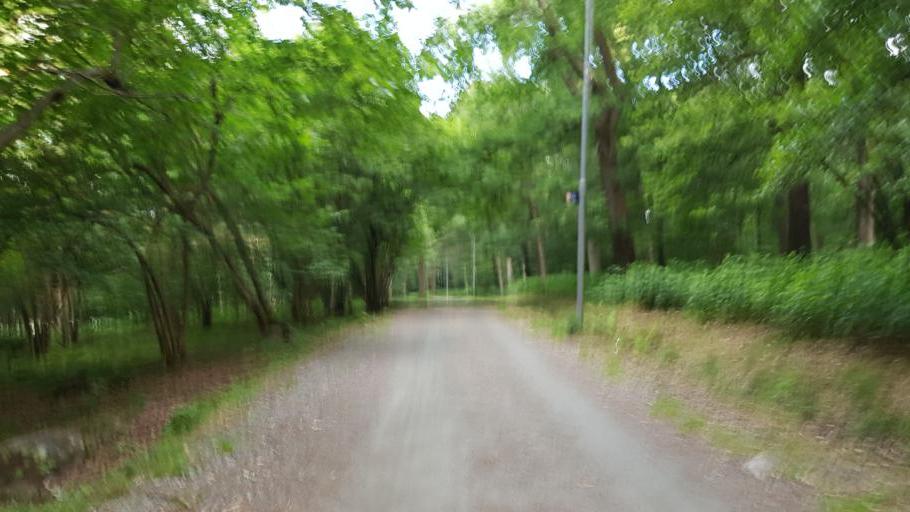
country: SE
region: Vaestra Goetaland
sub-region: Harryda Kommun
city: Molnlycke
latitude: 57.6596
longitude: 12.1014
